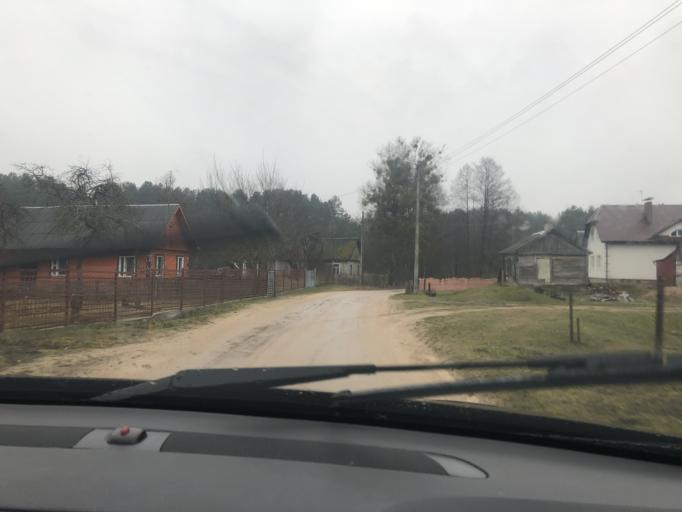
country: BY
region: Grodnenskaya
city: Skidal'
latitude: 53.8590
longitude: 24.2417
